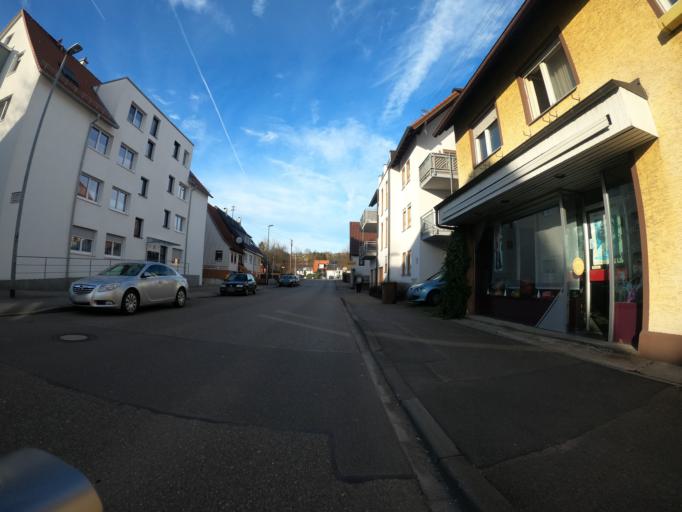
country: DE
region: Baden-Wuerttemberg
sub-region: Regierungsbezirk Stuttgart
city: Kirchheim unter Teck
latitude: 48.6586
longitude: 9.4228
